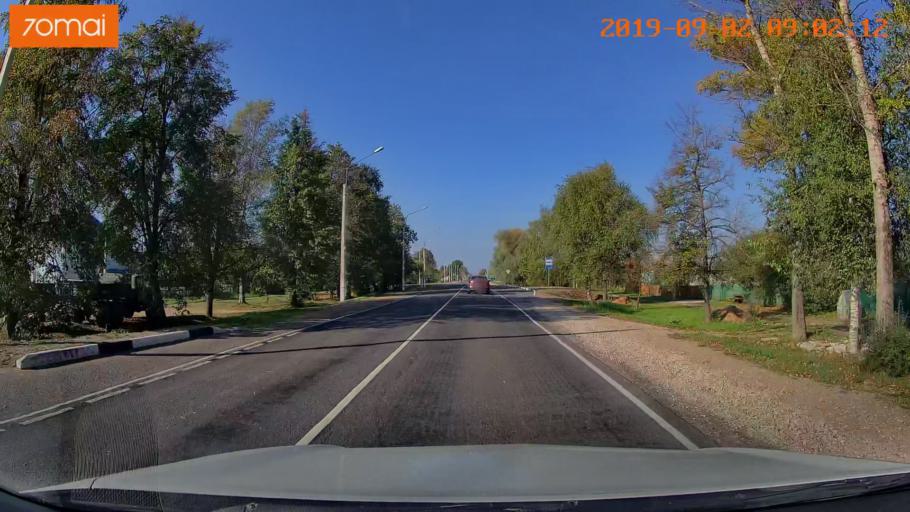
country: RU
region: Kaluga
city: Myatlevo
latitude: 54.9020
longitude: 35.6759
